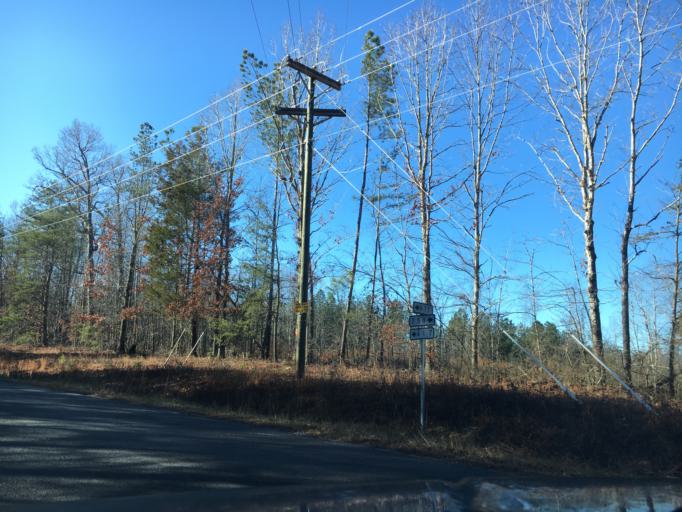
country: US
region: Virginia
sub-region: Fauquier County
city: Bealeton
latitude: 38.4789
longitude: -77.6500
